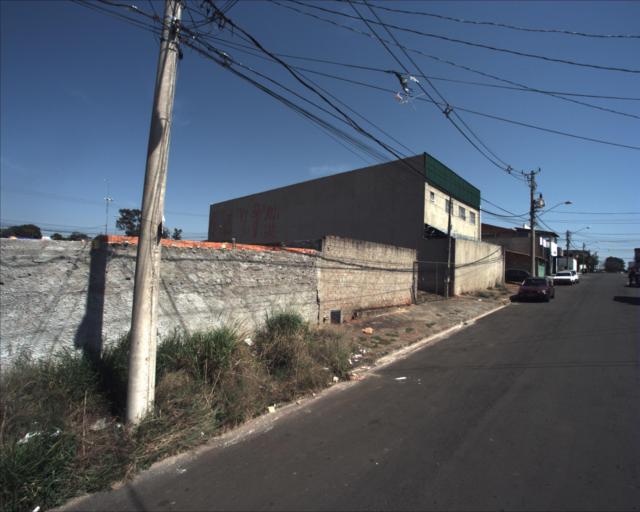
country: BR
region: Sao Paulo
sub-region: Sorocaba
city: Sorocaba
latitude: -23.4666
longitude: -47.4938
